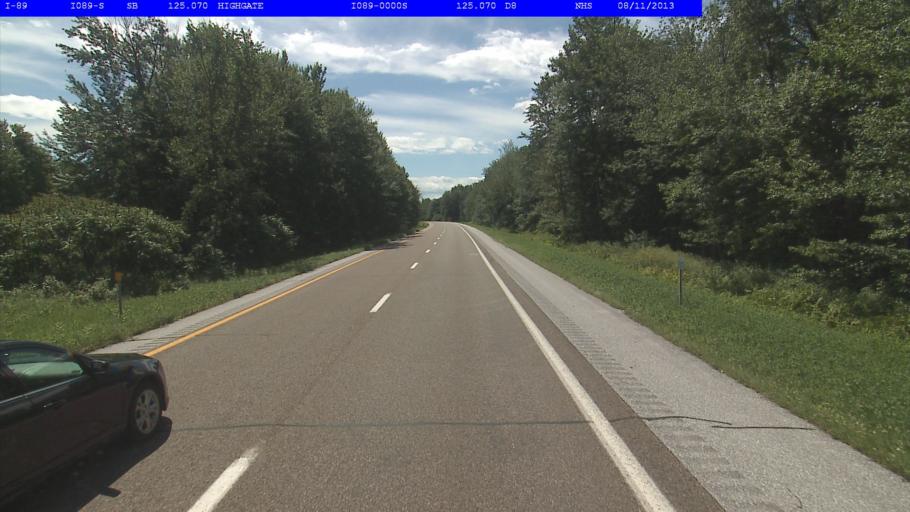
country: US
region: Vermont
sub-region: Franklin County
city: Swanton
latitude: 44.9460
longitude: -73.1142
